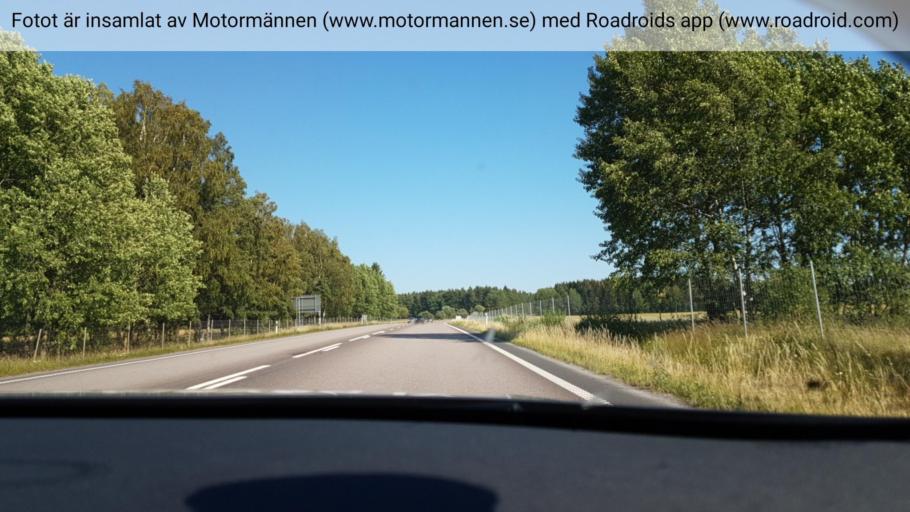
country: SE
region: Vaestra Goetaland
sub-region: Lidkopings Kommun
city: Vinninga
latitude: 58.4381
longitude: 13.2732
